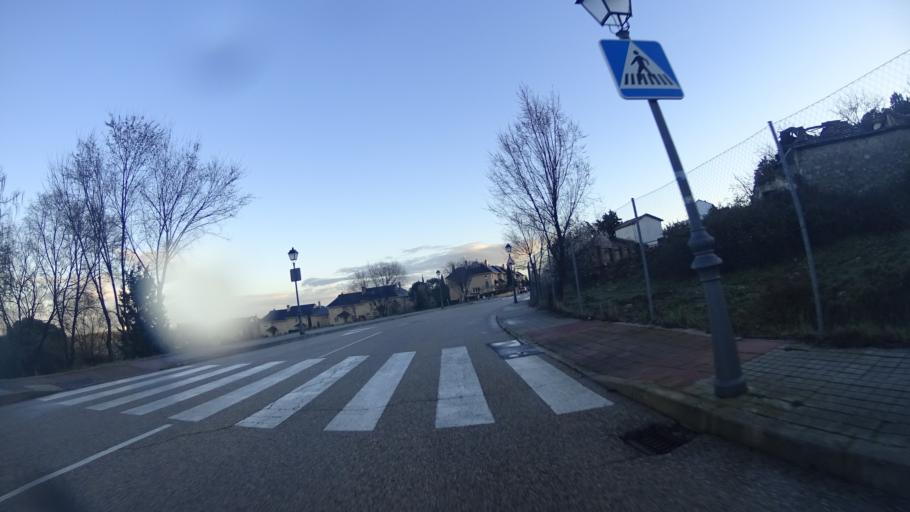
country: ES
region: Madrid
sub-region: Provincia de Madrid
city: Torrelodones
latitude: 40.5777
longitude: -3.9183
